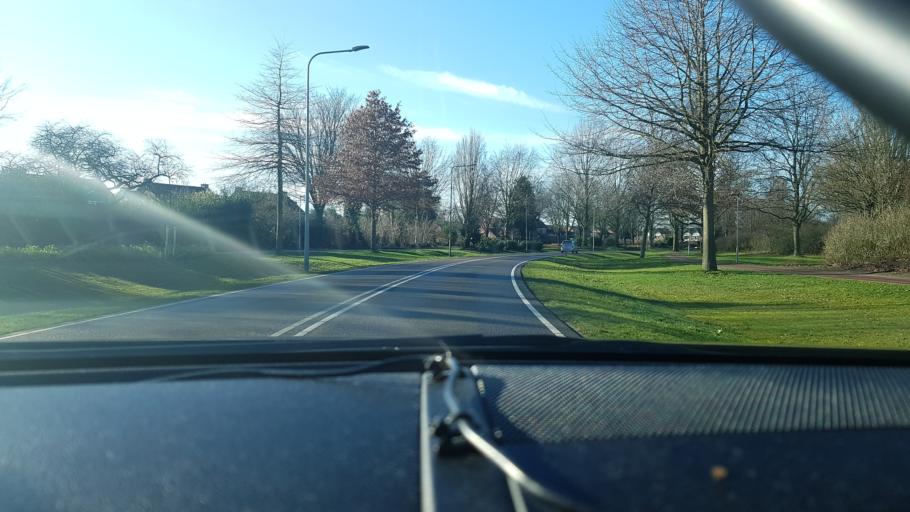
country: NL
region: Limburg
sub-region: Gemeente Peel en Maas
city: Maasbree
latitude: 51.3208
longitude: 5.9896
